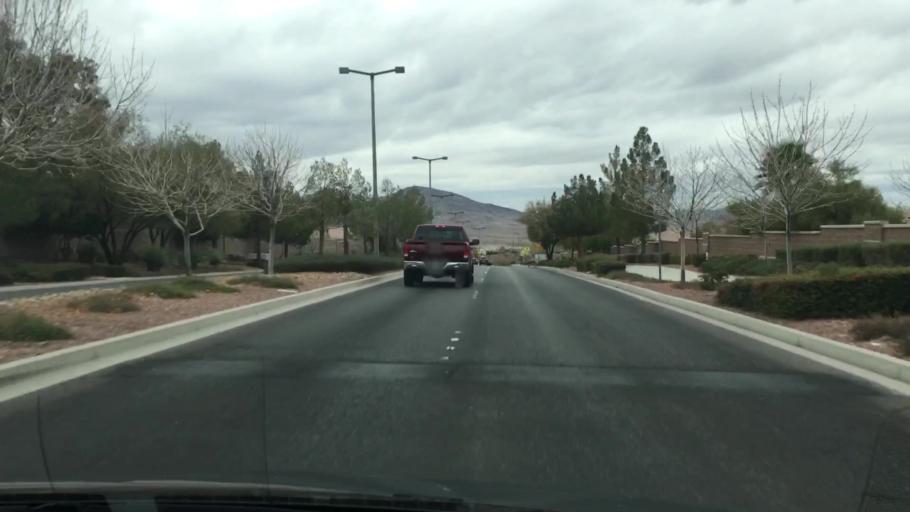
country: US
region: Nevada
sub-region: Clark County
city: Whitney
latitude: 35.9439
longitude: -115.1006
